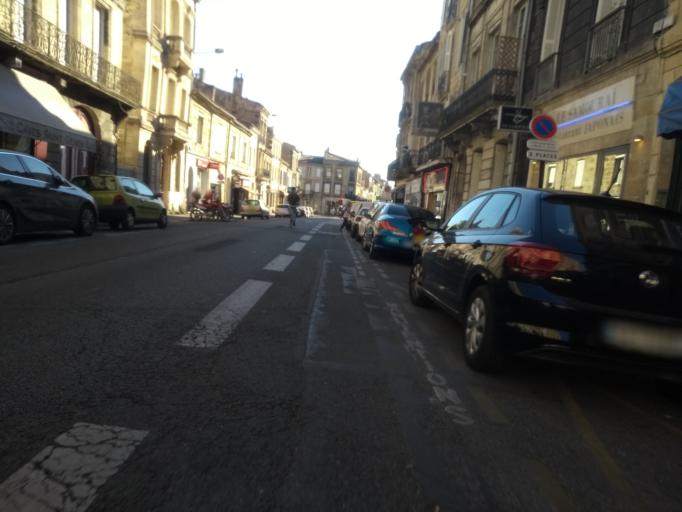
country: FR
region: Aquitaine
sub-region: Departement de la Gironde
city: Bordeaux
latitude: 44.8318
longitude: -0.5779
